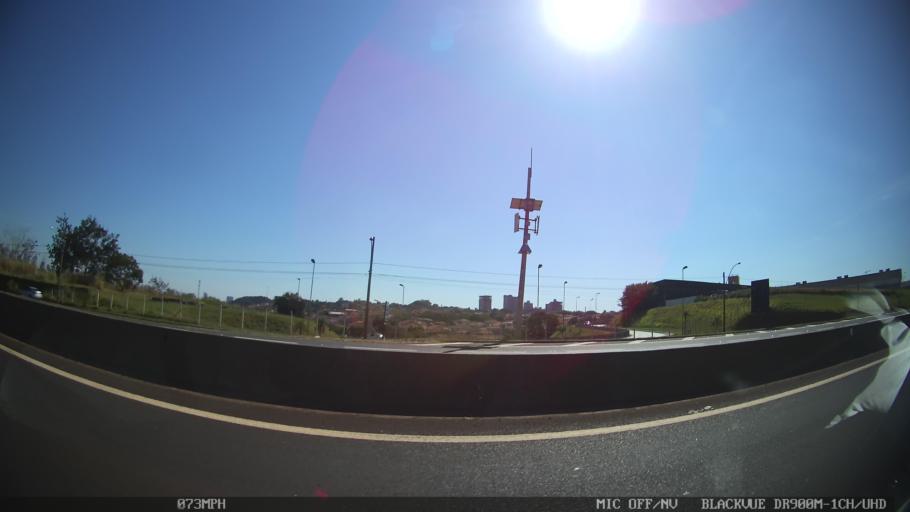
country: BR
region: Sao Paulo
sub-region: Ribeirao Preto
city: Ribeirao Preto
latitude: -21.2114
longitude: -47.7704
